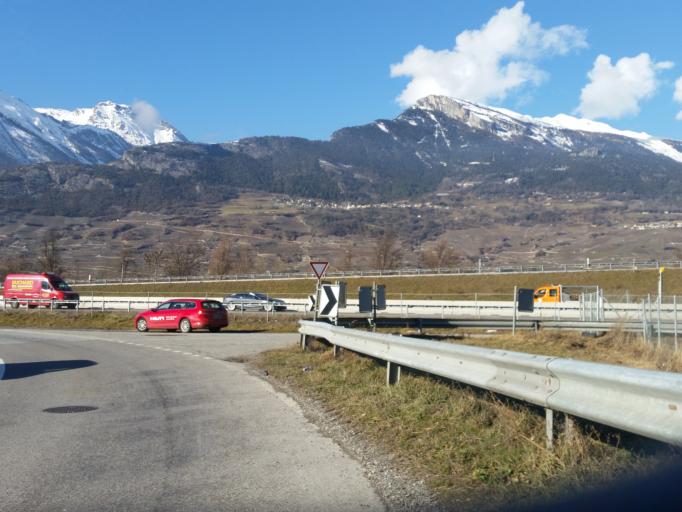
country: CH
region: Valais
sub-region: Conthey District
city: Vetroz
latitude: 46.2119
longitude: 7.2907
